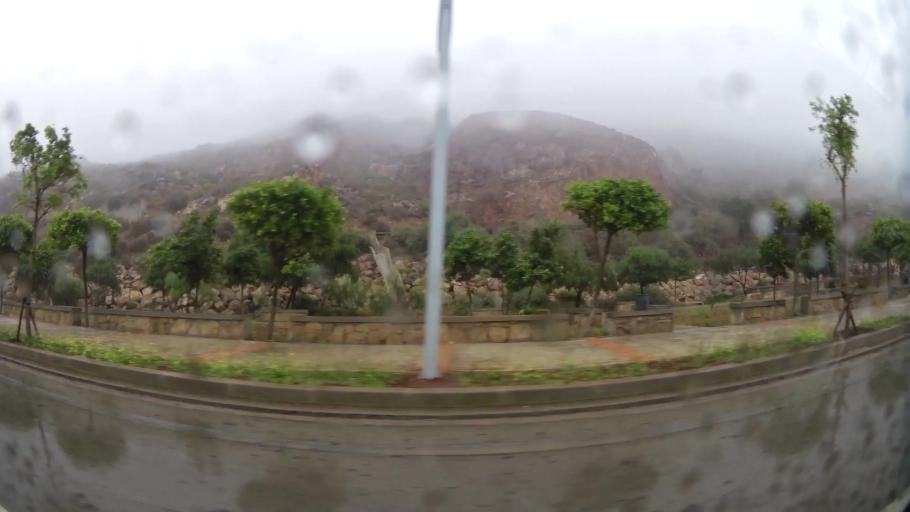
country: MA
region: Taza-Al Hoceima-Taounate
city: Tirhanimine
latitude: 35.2354
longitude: -3.9434
